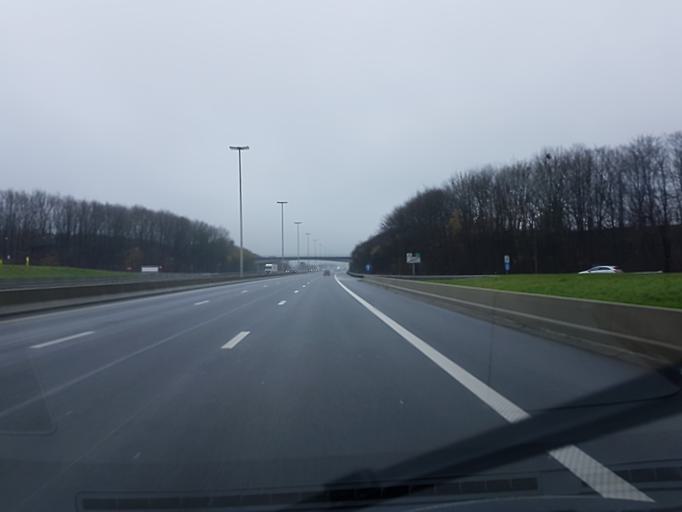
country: BE
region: Wallonia
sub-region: Province de Liege
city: Verlaine
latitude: 50.5927
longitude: 5.3020
